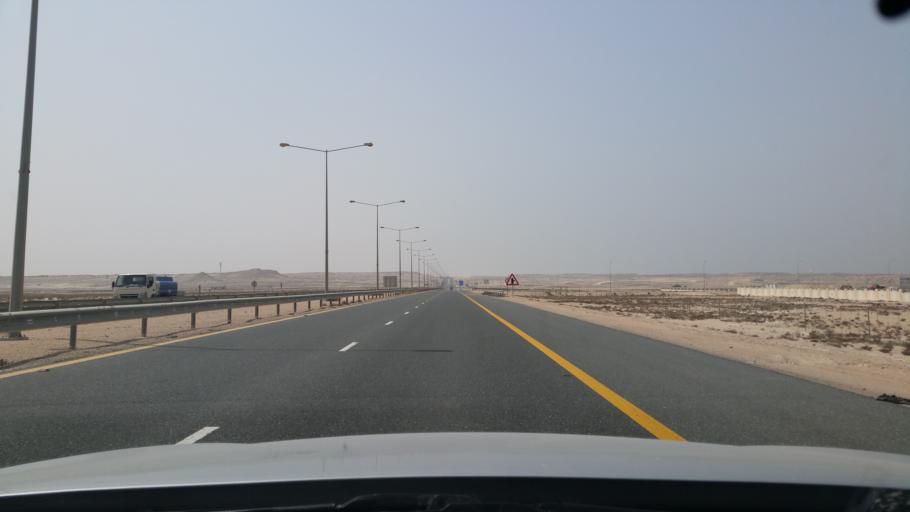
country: QA
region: Baladiyat ar Rayyan
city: Dukhan
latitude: 25.3774
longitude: 50.7812
